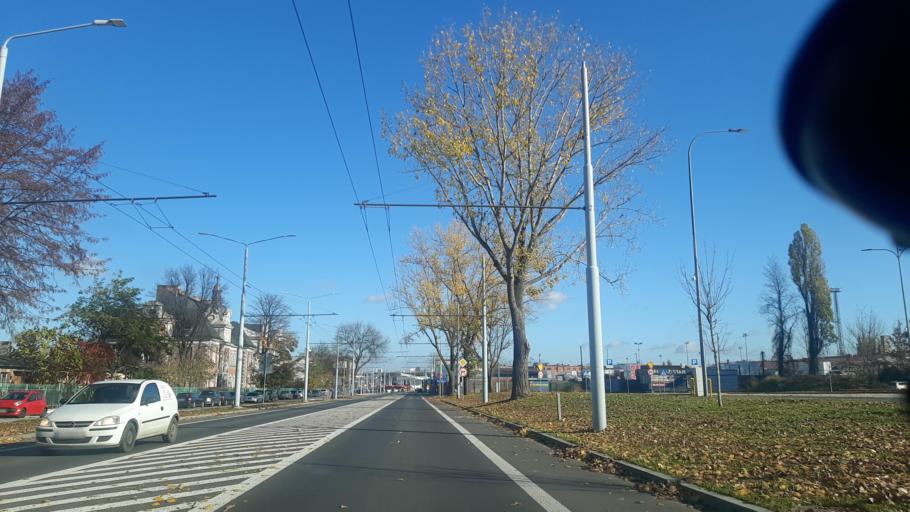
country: PL
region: Lublin Voivodeship
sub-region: Powiat lubelski
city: Lublin
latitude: 51.2290
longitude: 22.5597
